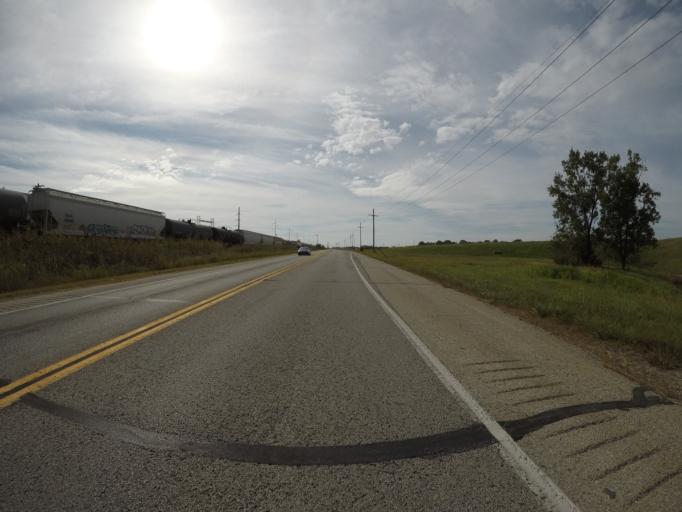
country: US
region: Kansas
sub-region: Johnson County
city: Gardner
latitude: 38.8136
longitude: -94.8970
